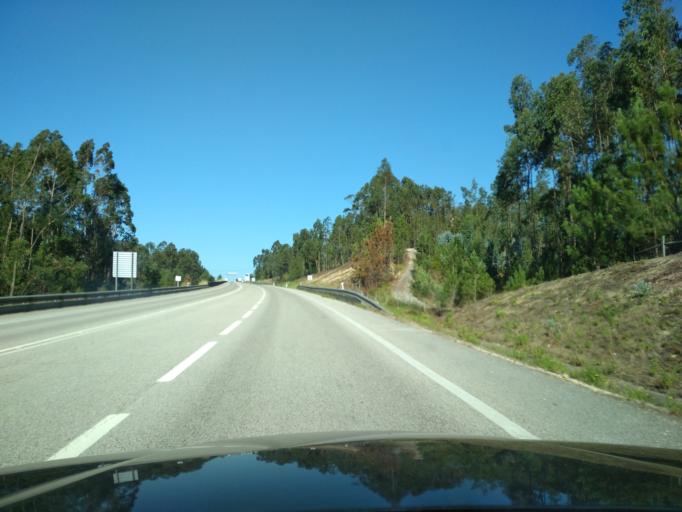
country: PT
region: Leiria
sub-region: Pombal
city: Lourical
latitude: 39.9878
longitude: -8.7701
